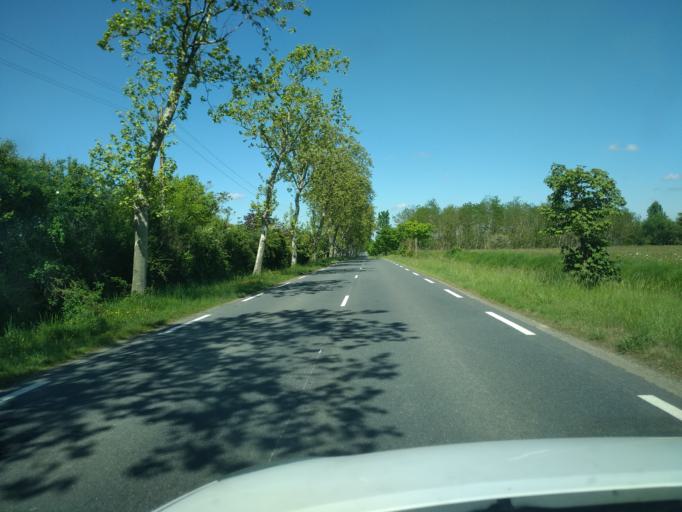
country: FR
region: Midi-Pyrenees
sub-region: Departement de la Haute-Garonne
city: Boulogne-sur-Gesse
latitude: 43.2975
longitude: 0.6689
